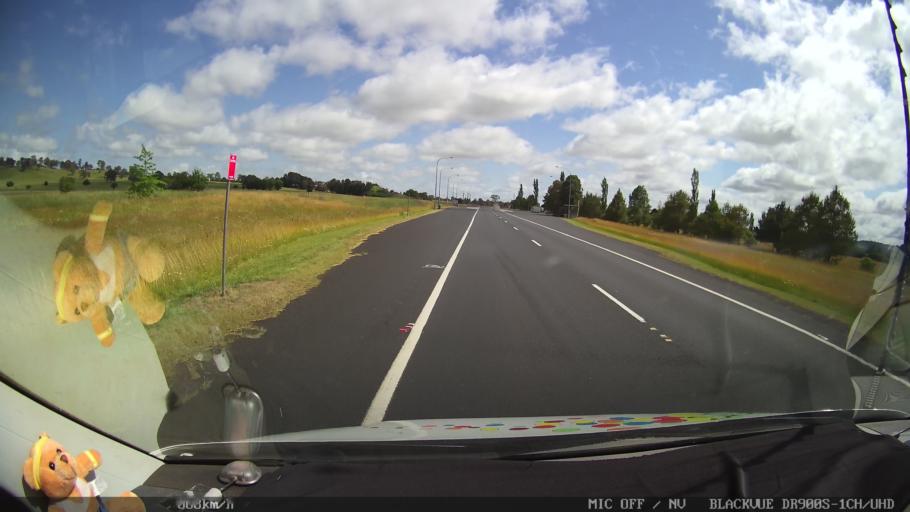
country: AU
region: New South Wales
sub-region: Glen Innes Severn
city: Glen Innes
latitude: -29.9242
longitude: 151.7241
